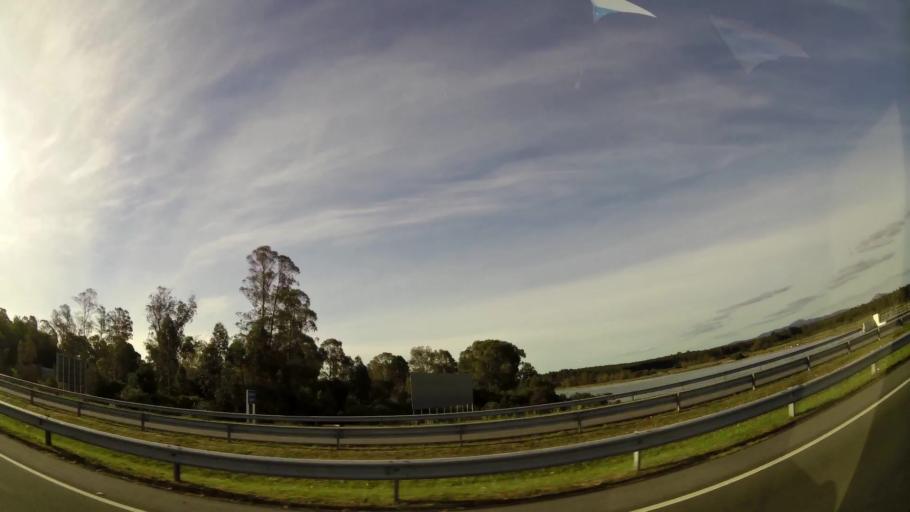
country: UY
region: Maldonado
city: Piriapolis
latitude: -34.7796
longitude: -55.3979
